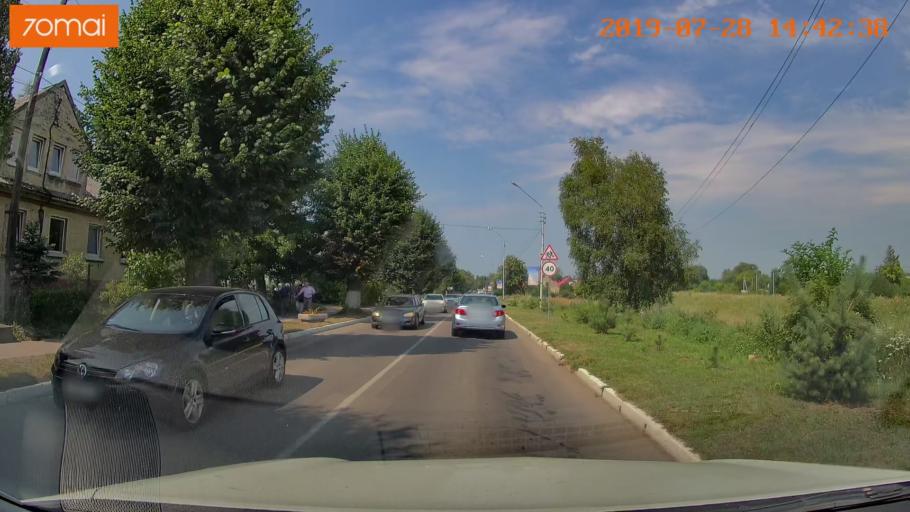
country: RU
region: Kaliningrad
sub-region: Gorod Kaliningrad
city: Yantarnyy
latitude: 54.8611
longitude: 19.9413
